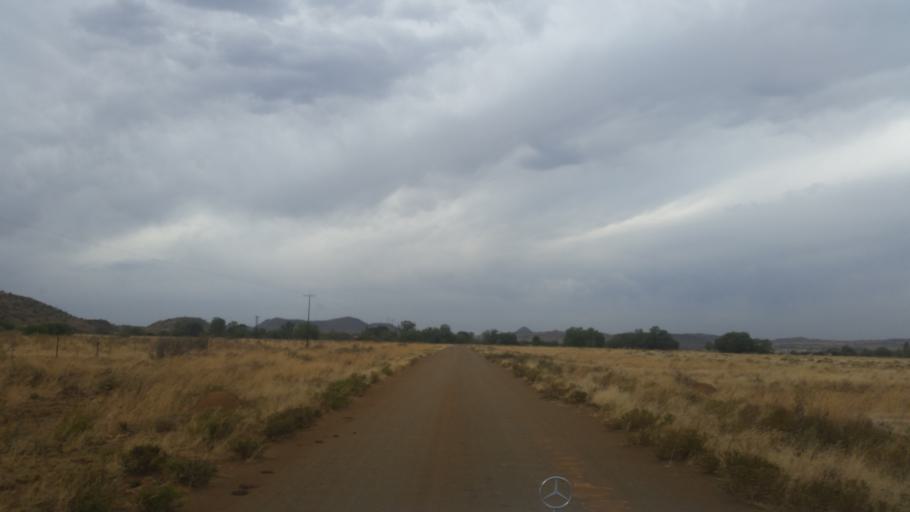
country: ZA
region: Orange Free State
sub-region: Xhariep District Municipality
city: Trompsburg
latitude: -30.5013
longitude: 25.9547
